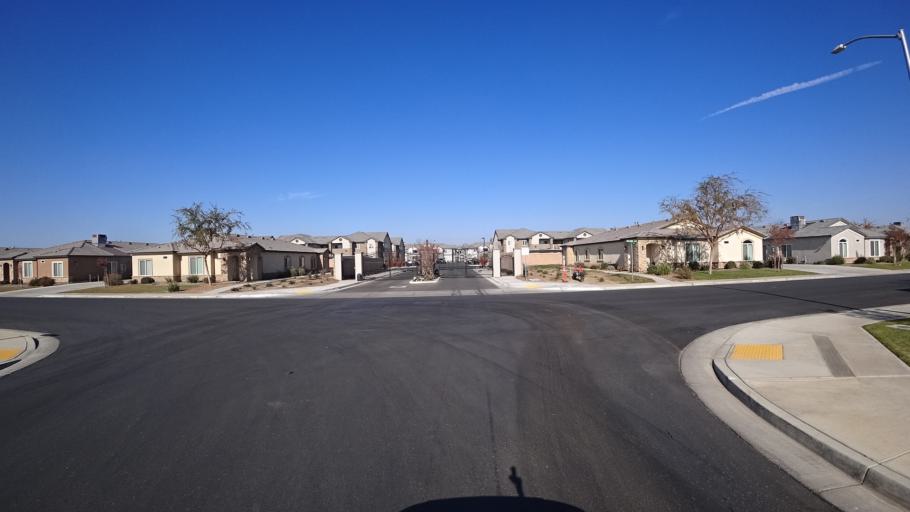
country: US
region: California
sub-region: Kern County
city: Greenfield
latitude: 35.2924
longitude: -119.0600
